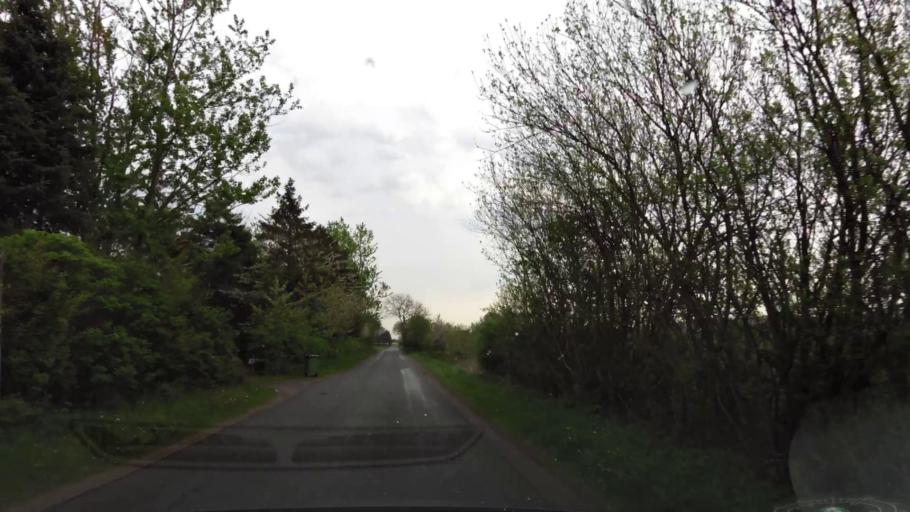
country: DK
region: South Denmark
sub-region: Faaborg-Midtfyn Kommune
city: Ringe
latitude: 55.1920
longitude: 10.5512
